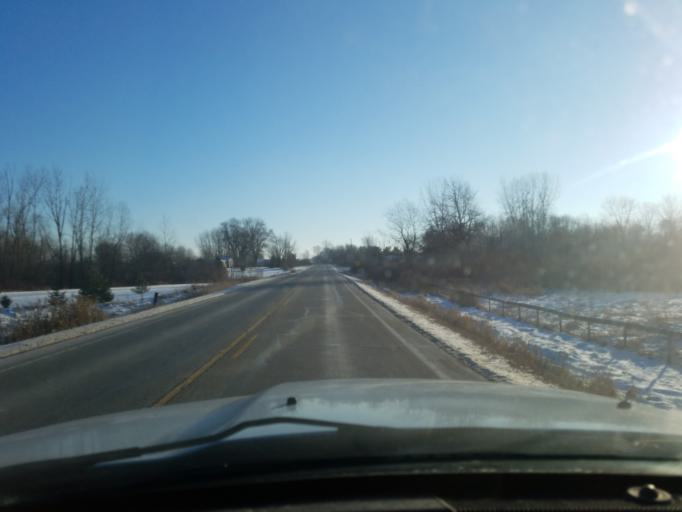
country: US
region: Indiana
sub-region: Noble County
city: Ligonier
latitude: 41.4524
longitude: -85.5568
